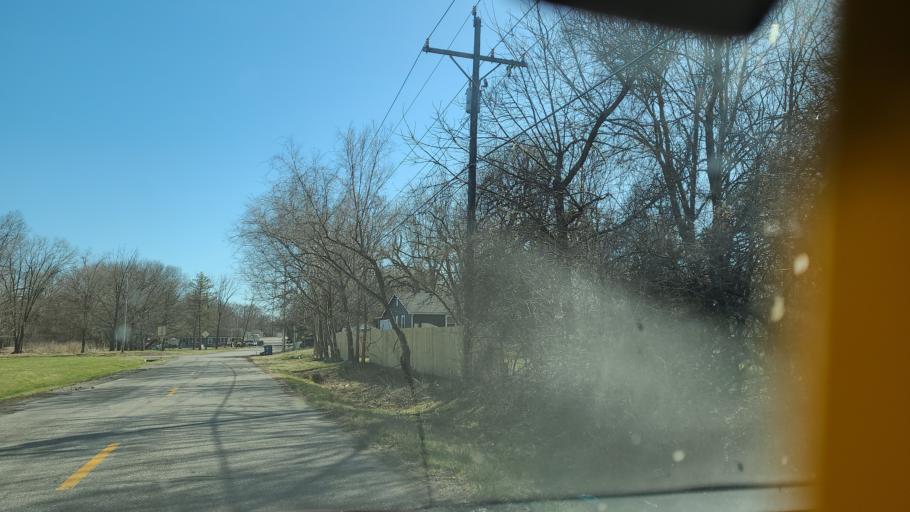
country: US
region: Kansas
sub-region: Douglas County
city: Lawrence
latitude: 38.9814
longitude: -95.2239
